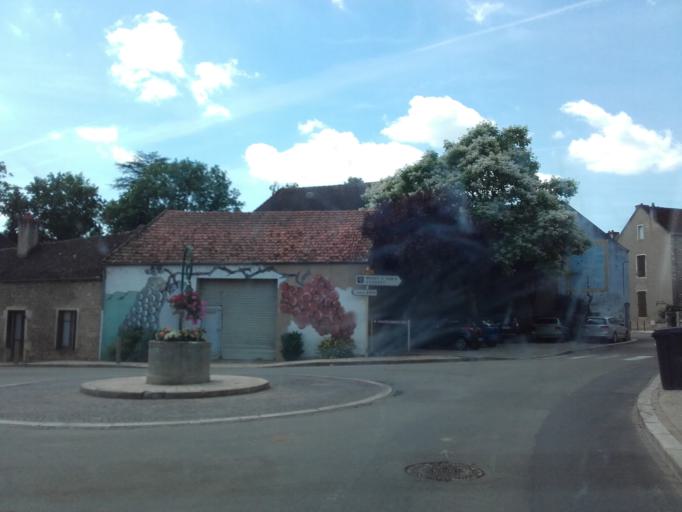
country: FR
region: Bourgogne
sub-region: Departement de la Cote-d'Or
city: Gevrey-Chambertin
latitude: 47.2246
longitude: 4.9707
